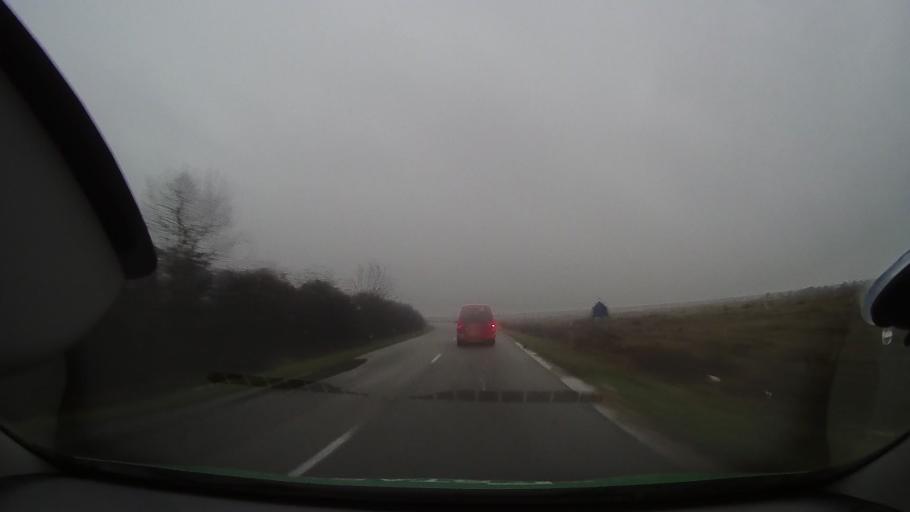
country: RO
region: Arad
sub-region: Comuna Craiova
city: Craiova
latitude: 46.6142
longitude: 21.9567
